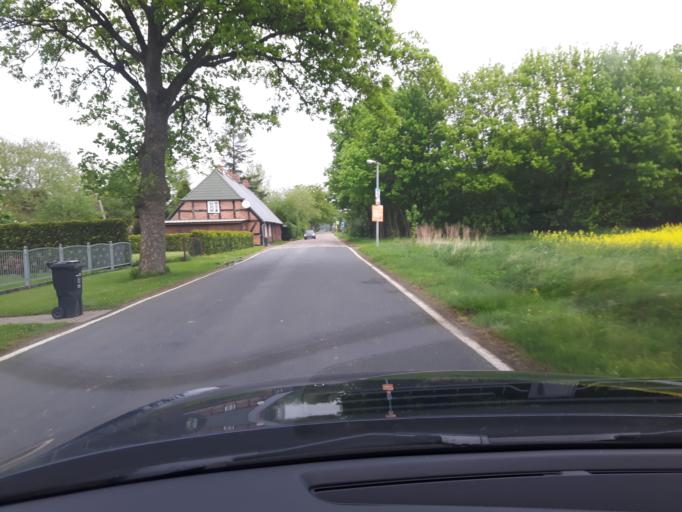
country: DE
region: Mecklenburg-Vorpommern
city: Velgast
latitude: 54.2155
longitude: 12.7341
